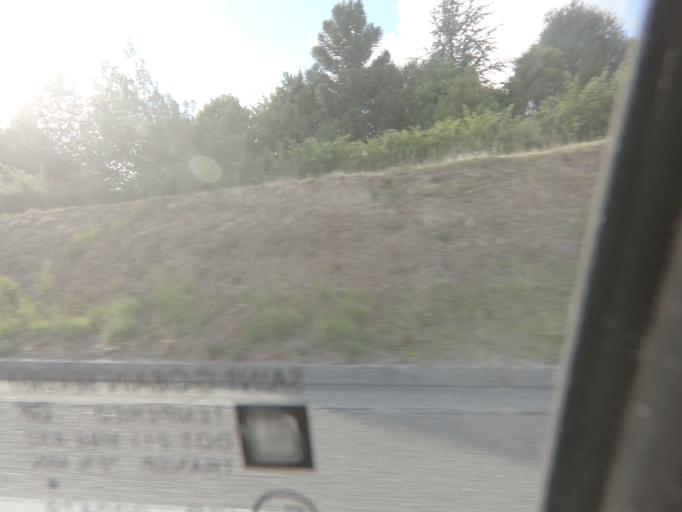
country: PT
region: Porto
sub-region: Lousada
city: Meinedo
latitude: 41.2321
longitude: -8.2100
